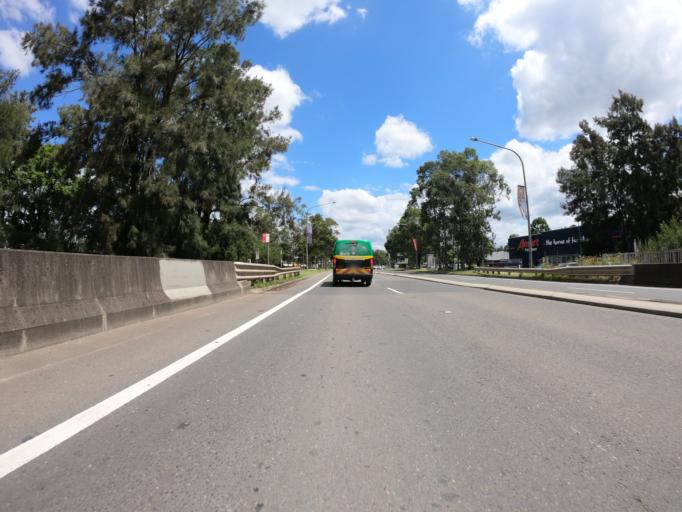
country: AU
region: New South Wales
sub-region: Penrith Municipality
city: Glenmore Park
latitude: -33.7679
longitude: 150.6780
